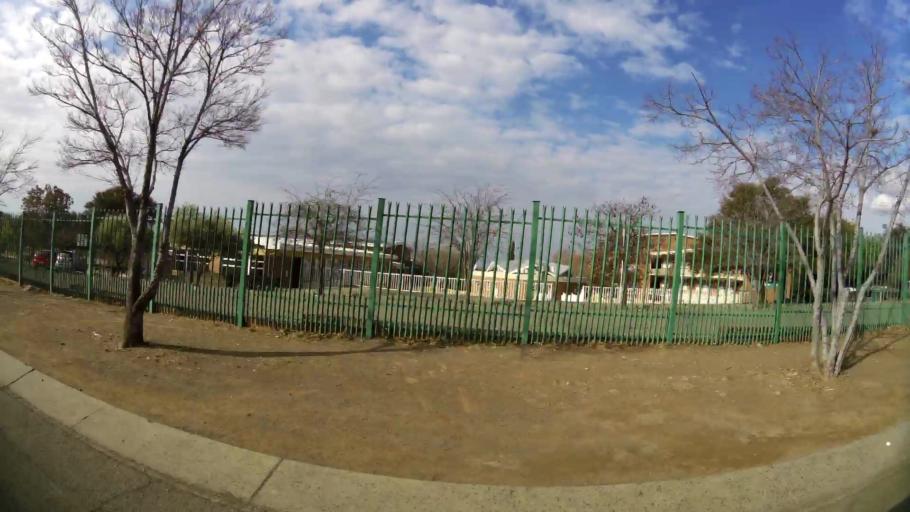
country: ZA
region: Orange Free State
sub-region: Mangaung Metropolitan Municipality
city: Bloemfontein
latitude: -29.0762
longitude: 26.2314
